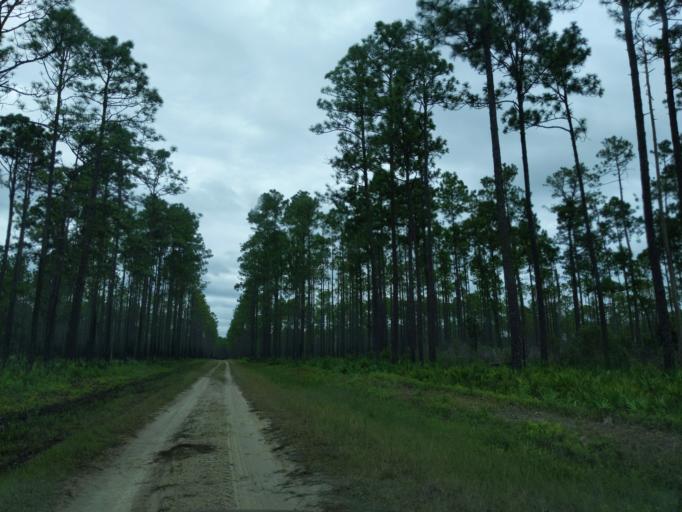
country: US
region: Florida
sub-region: Gadsden County
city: Midway
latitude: 30.3716
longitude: -84.4863
